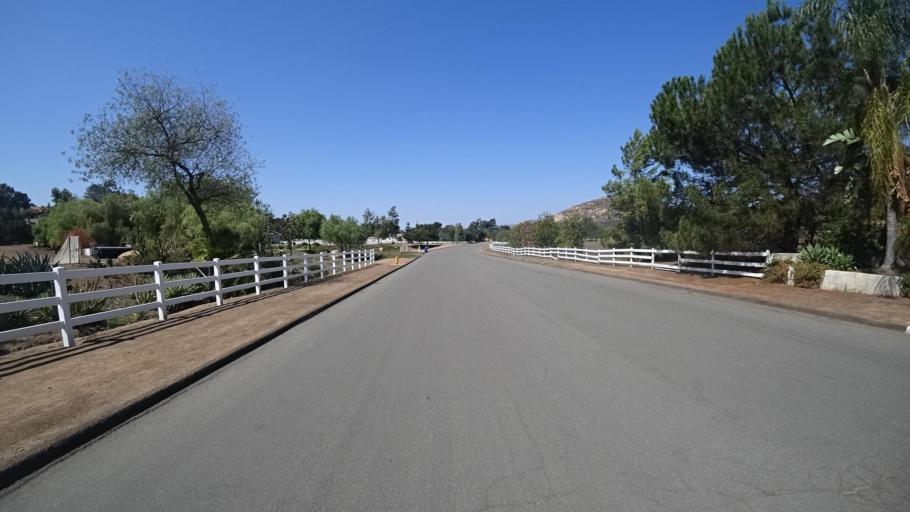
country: US
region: California
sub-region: San Diego County
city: Crest
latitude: 32.8259
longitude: -116.8547
